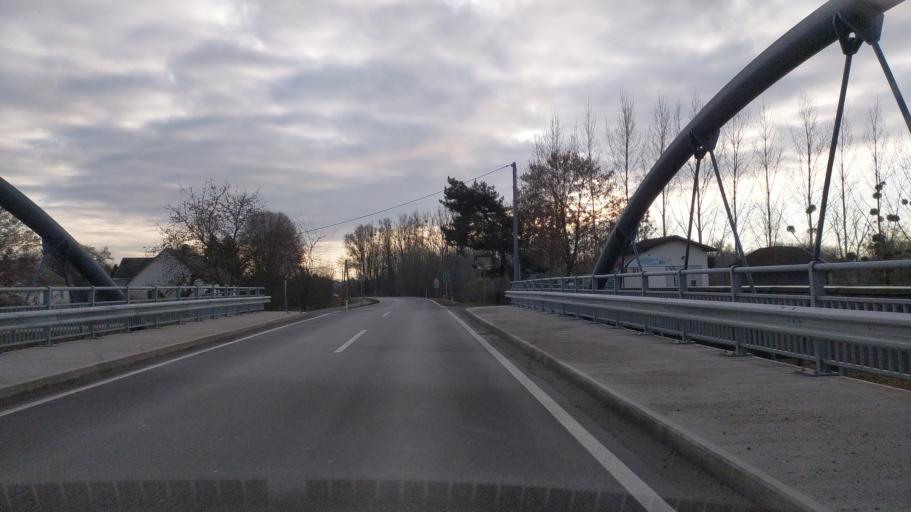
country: AT
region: Upper Austria
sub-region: Politischer Bezirk Perg
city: Perg
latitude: 48.2373
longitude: 14.5664
